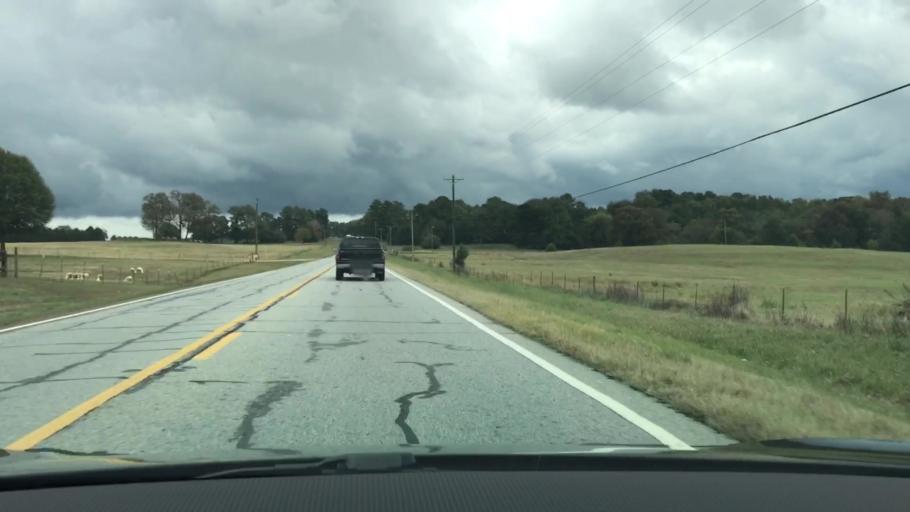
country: US
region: Georgia
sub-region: Oconee County
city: Watkinsville
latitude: 33.7946
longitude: -83.3281
